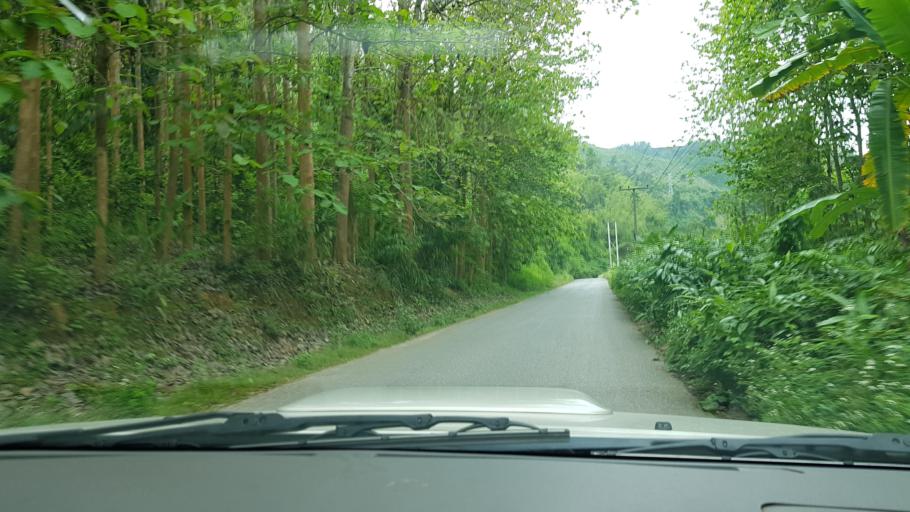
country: LA
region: Phongsali
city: Khoa
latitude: 21.0810
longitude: 102.3725
